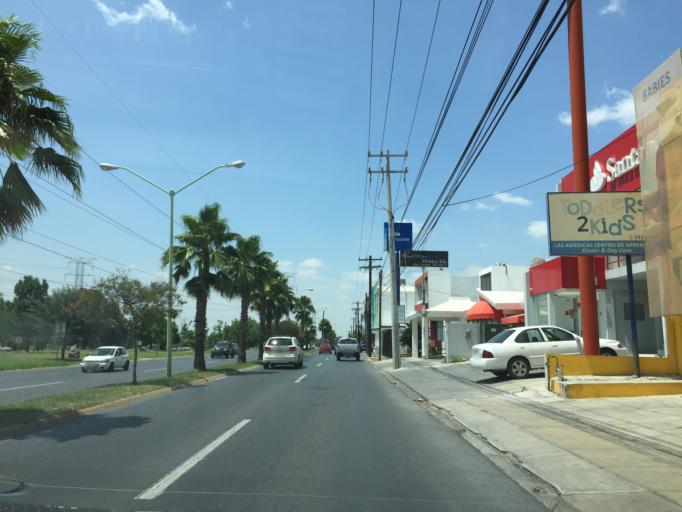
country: MX
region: Nuevo Leon
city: Guadalupe
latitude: 25.6432
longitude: -100.2685
